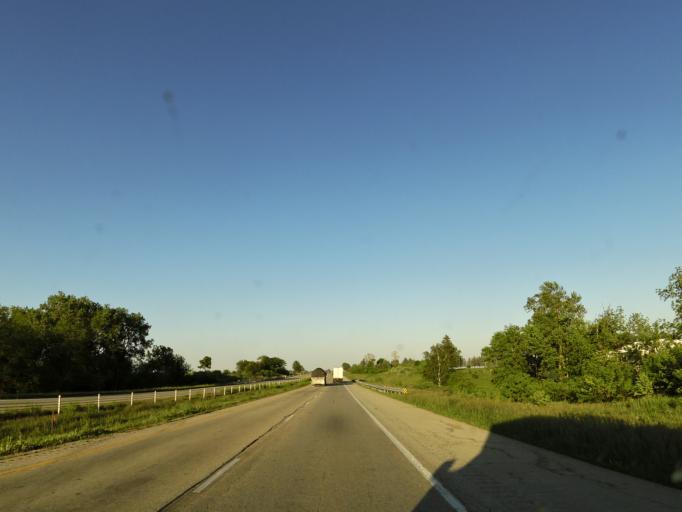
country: US
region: Illinois
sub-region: Vermilion County
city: Oakwood
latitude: 40.1245
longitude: -87.8352
